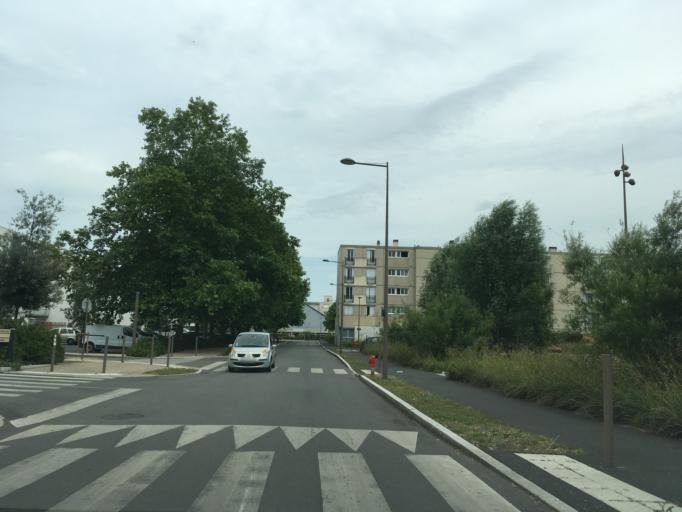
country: FR
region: Poitou-Charentes
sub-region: Departement des Deux-Sevres
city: Niort
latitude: 46.3155
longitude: -0.4807
